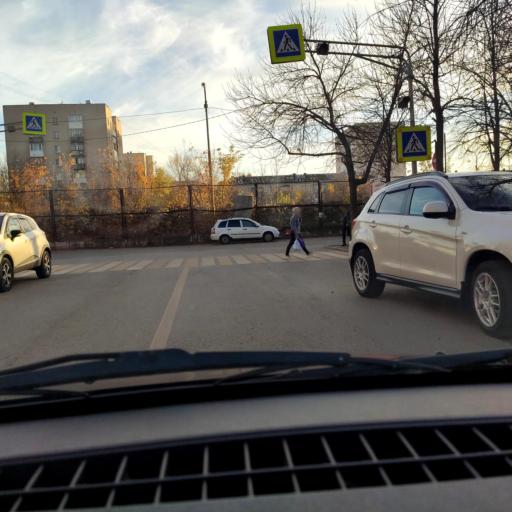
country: RU
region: Bashkortostan
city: Ufa
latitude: 54.7783
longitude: 56.0267
